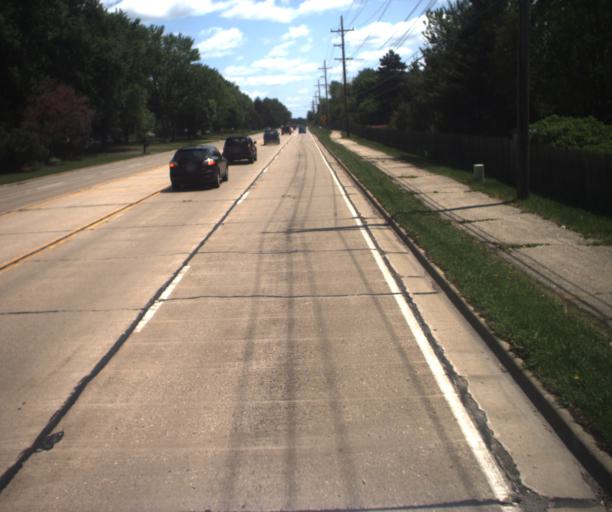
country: US
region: Illinois
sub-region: Kane County
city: Batavia
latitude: 41.8639
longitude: -88.3257
